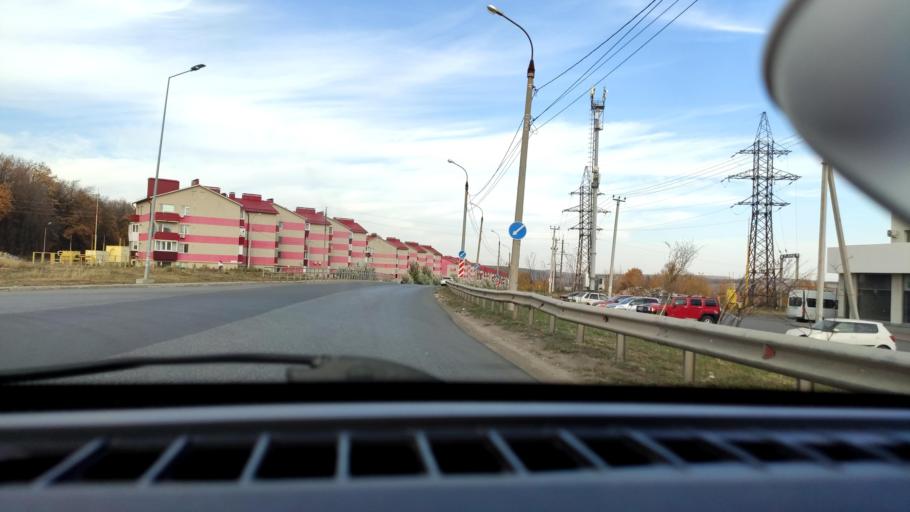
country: RU
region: Samara
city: Novosemeykino
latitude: 53.3275
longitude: 50.3113
